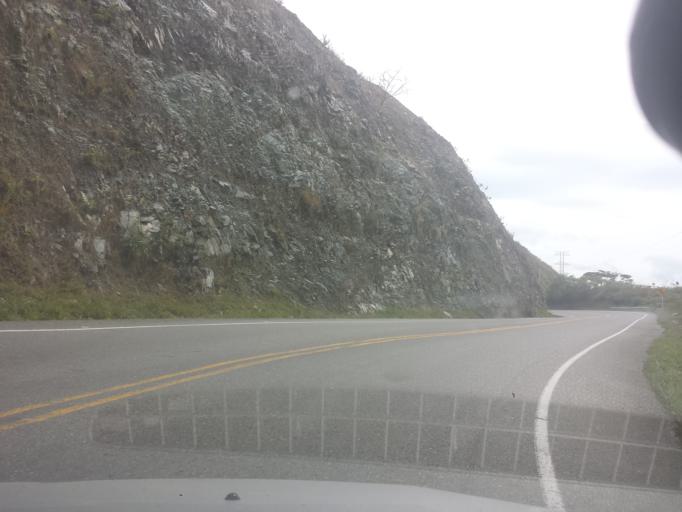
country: CO
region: Antioquia
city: Liborina
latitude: 6.6254
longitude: -75.8743
